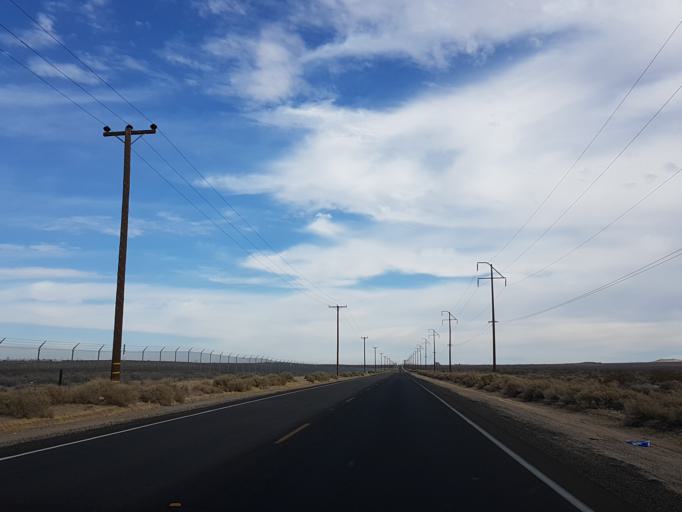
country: US
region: California
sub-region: Kern County
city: Ridgecrest
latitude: 35.6225
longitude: -117.6295
